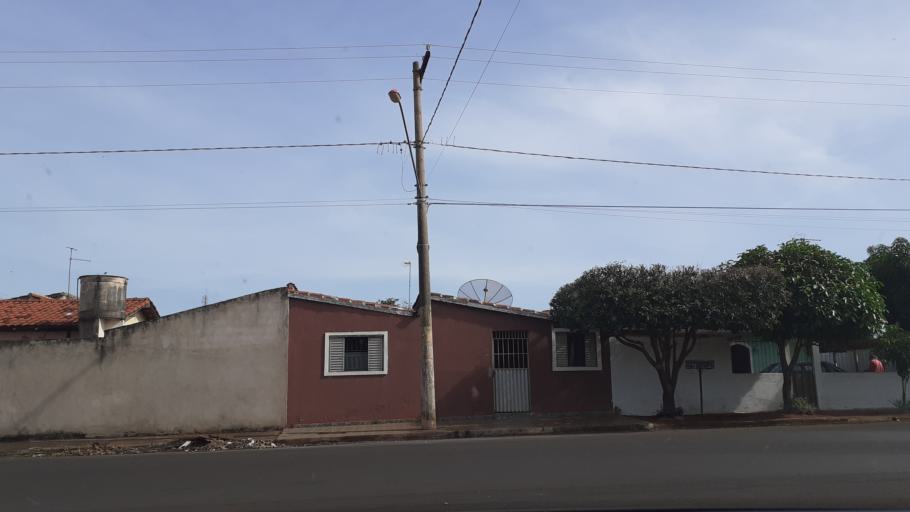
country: BR
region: Goias
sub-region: Itumbiara
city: Itumbiara
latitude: -18.4168
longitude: -49.2411
